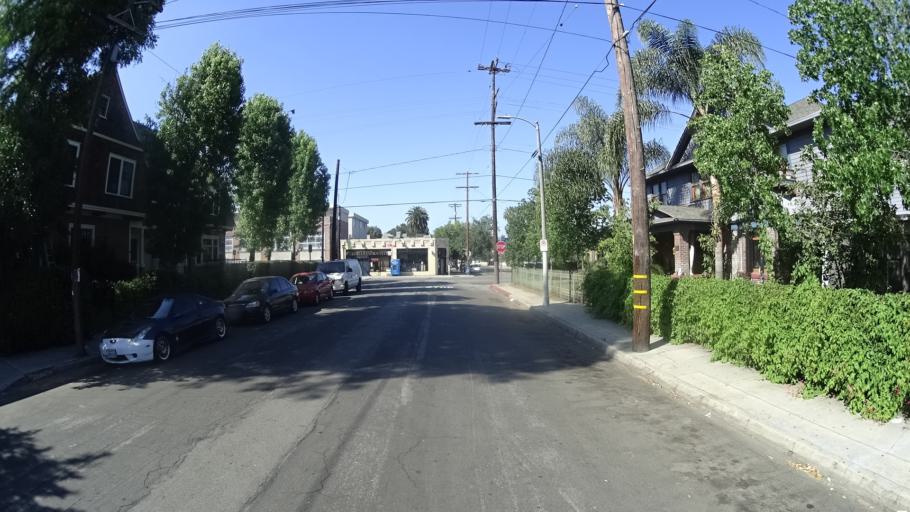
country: US
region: California
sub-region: Los Angeles County
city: Los Angeles
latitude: 34.0341
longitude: -118.2807
